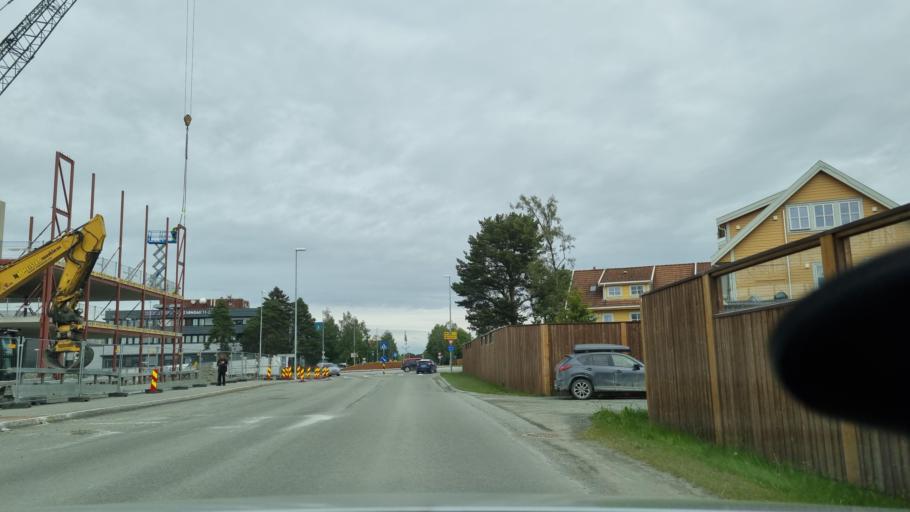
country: NO
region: Sor-Trondelag
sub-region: Trondheim
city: Trondheim
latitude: 63.3478
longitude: 10.3595
